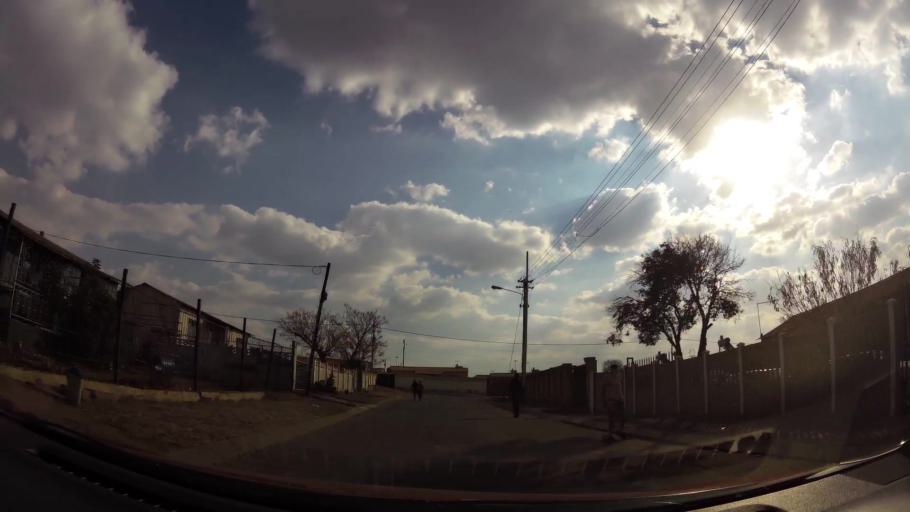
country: ZA
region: Gauteng
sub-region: City of Johannesburg Metropolitan Municipality
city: Soweto
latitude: -26.2304
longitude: 27.9401
